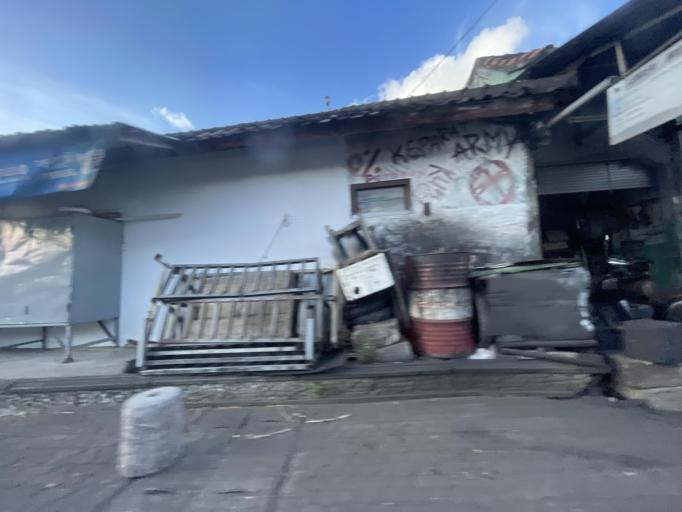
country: ID
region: Bali
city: Kelanabian
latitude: -8.7711
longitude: 115.1743
